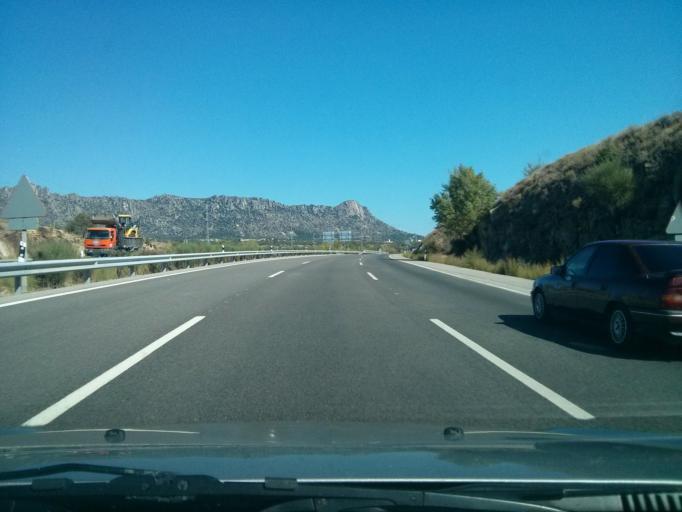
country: ES
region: Madrid
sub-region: Provincia de Madrid
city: Cabanillas de la Sierra
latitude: 40.8401
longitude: -3.6209
